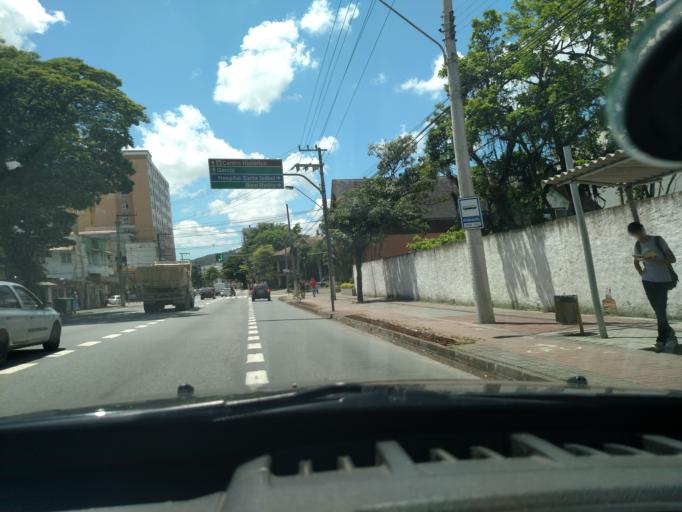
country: BR
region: Santa Catarina
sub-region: Blumenau
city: Blumenau
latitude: -26.9225
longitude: -49.0647
